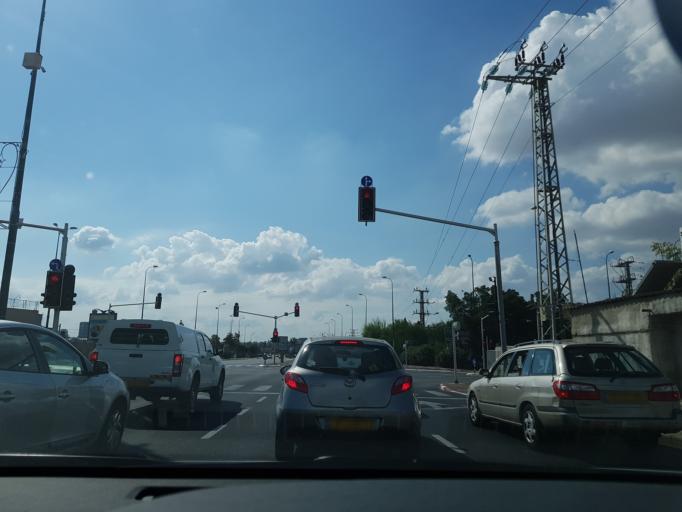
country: IL
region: Central District
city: Ness Ziona
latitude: 31.9246
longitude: 34.7978
